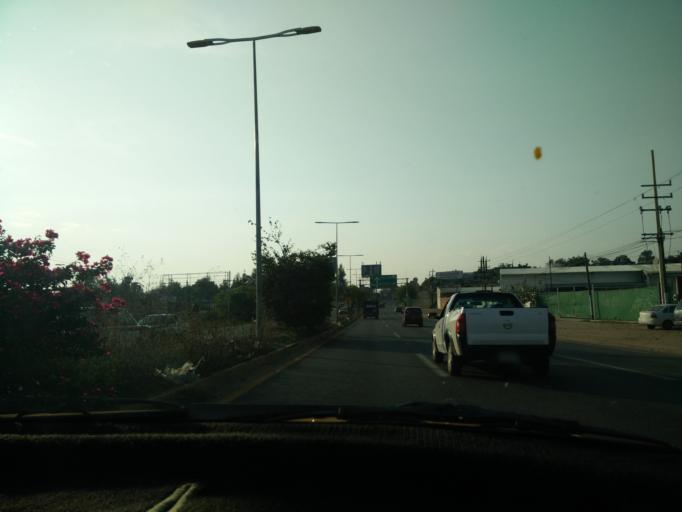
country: MX
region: Oaxaca
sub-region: Santa Maria Atzompa
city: Fraccionamiento Riberas de San Jeronimo
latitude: 17.1332
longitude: -96.7730
